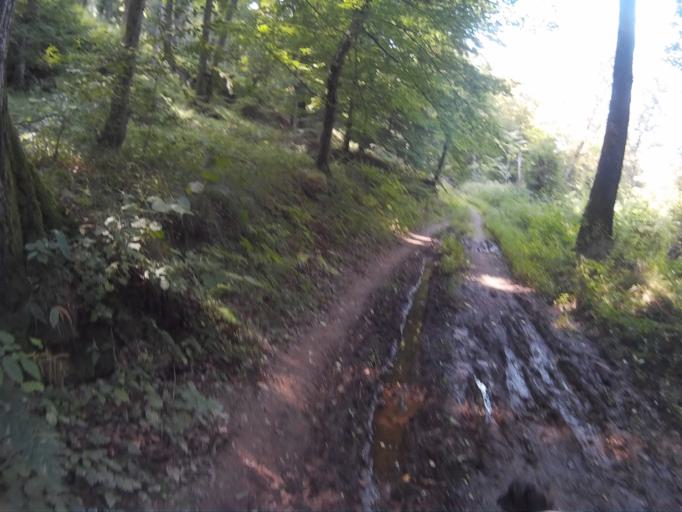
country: AT
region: Burgenland
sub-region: Politischer Bezirk Oberpullendorf
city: Mannersdorf an der Rabnitz
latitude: 47.4049
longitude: 16.5167
